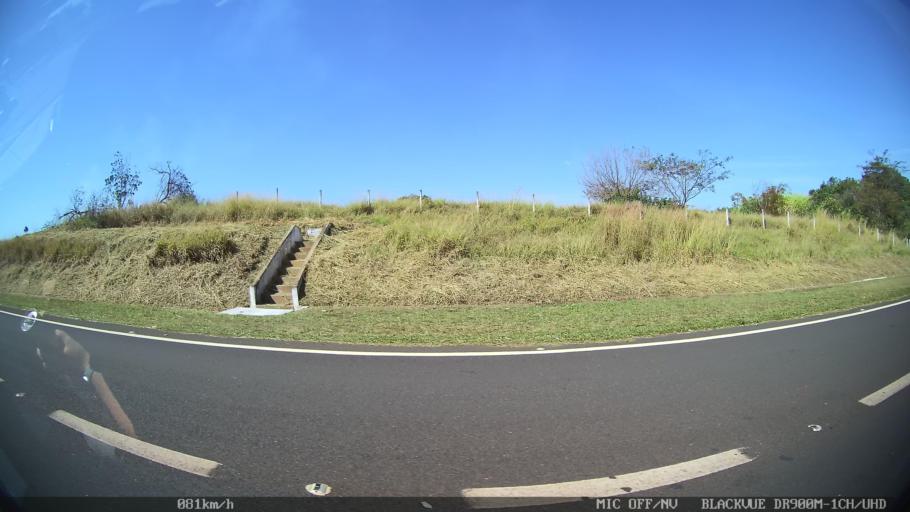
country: BR
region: Sao Paulo
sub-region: Batatais
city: Batatais
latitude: -20.8720
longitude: -47.6033
